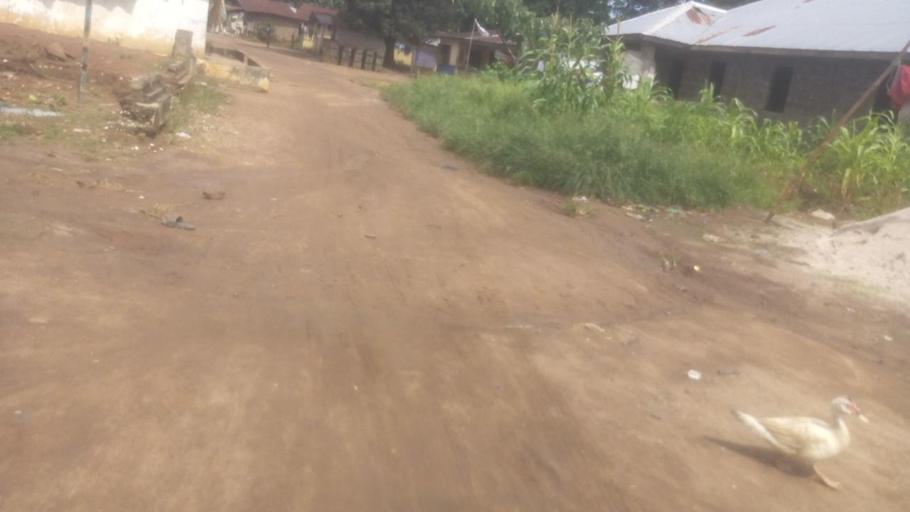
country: SL
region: Northern Province
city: Masoyila
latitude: 8.5889
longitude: -13.1972
